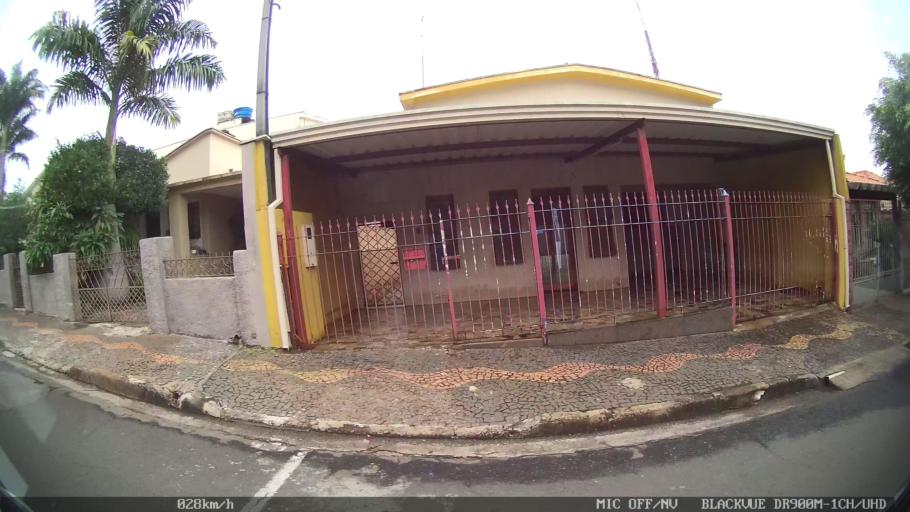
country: BR
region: Sao Paulo
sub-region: Americana
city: Americana
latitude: -22.7394
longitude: -47.3233
